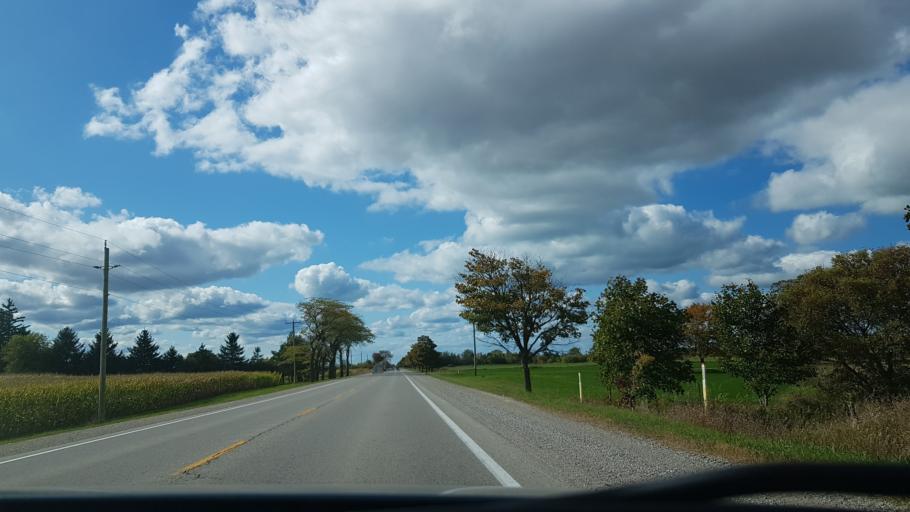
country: CA
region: Ontario
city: Bluewater
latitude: 43.3446
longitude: -81.6494
